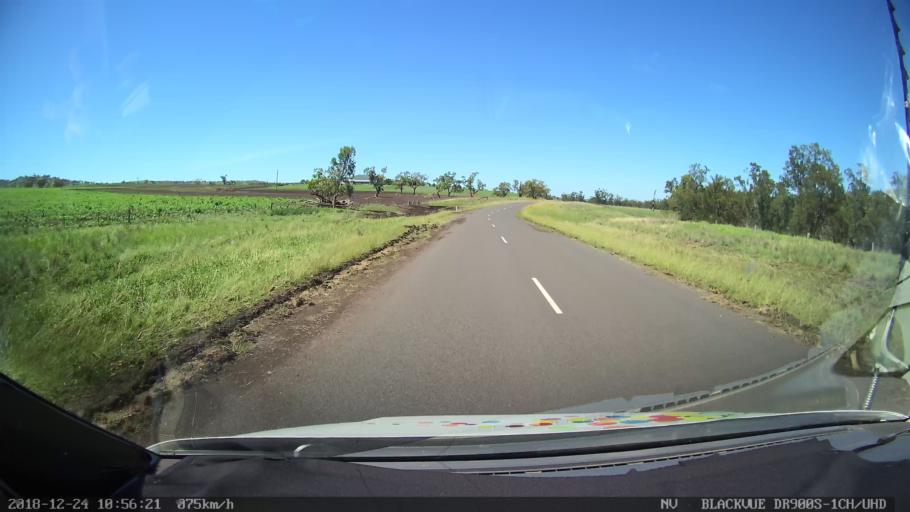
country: AU
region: New South Wales
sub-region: Upper Hunter Shire
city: Merriwa
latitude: -32.0247
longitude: 150.4185
